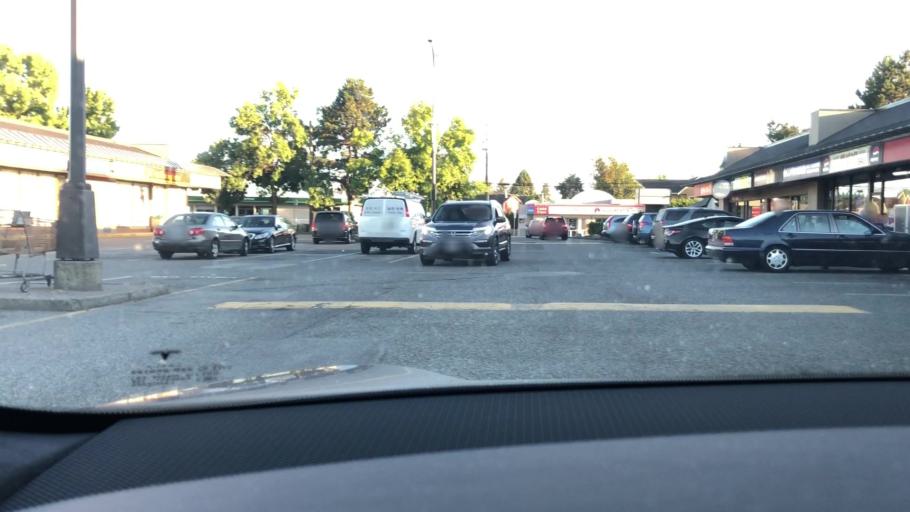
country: CA
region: British Columbia
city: Richmond
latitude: 49.1490
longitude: -123.1823
